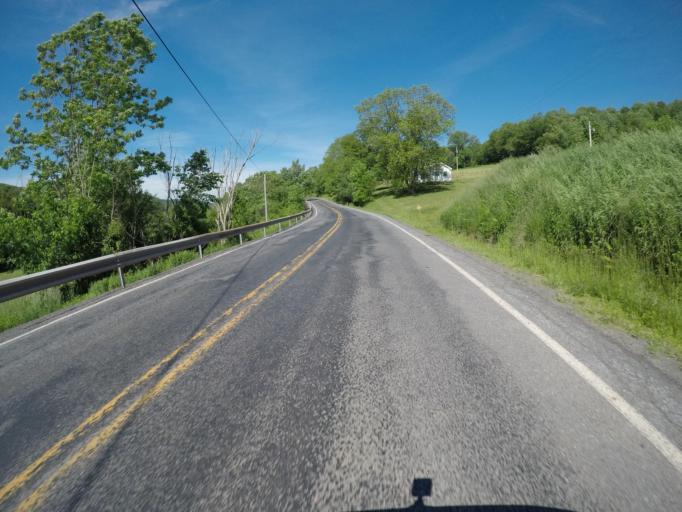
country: US
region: New York
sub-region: Delaware County
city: Delhi
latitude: 42.2124
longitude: -74.9366
